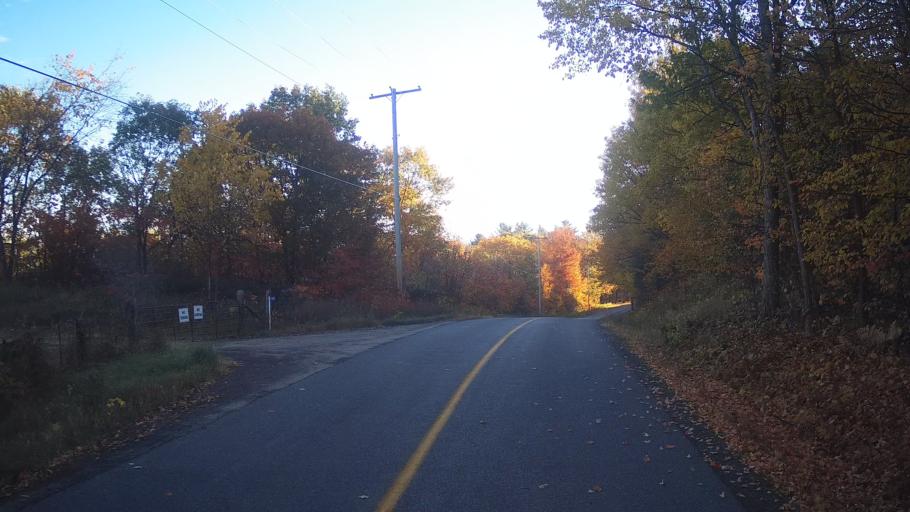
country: CA
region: Ontario
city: Arnprior
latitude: 45.3451
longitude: -76.3299
